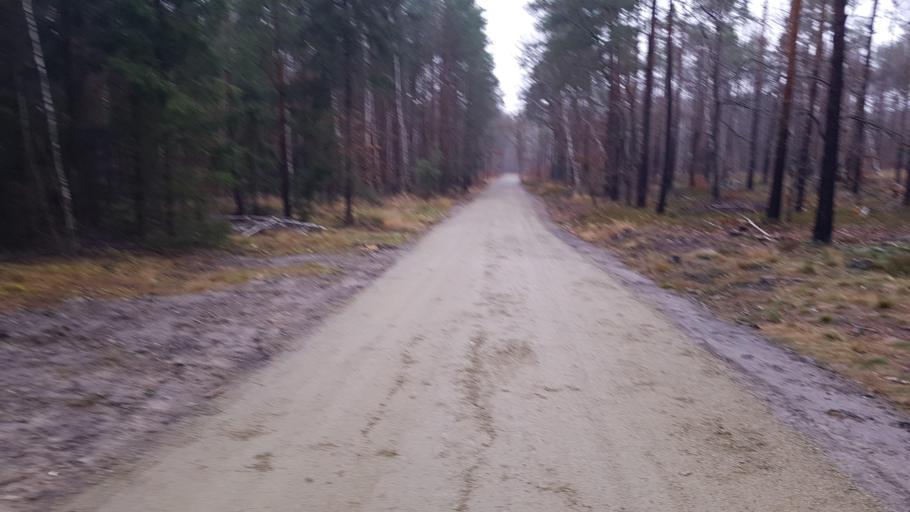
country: DE
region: Brandenburg
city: Finsterwalde
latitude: 51.6249
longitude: 13.6814
